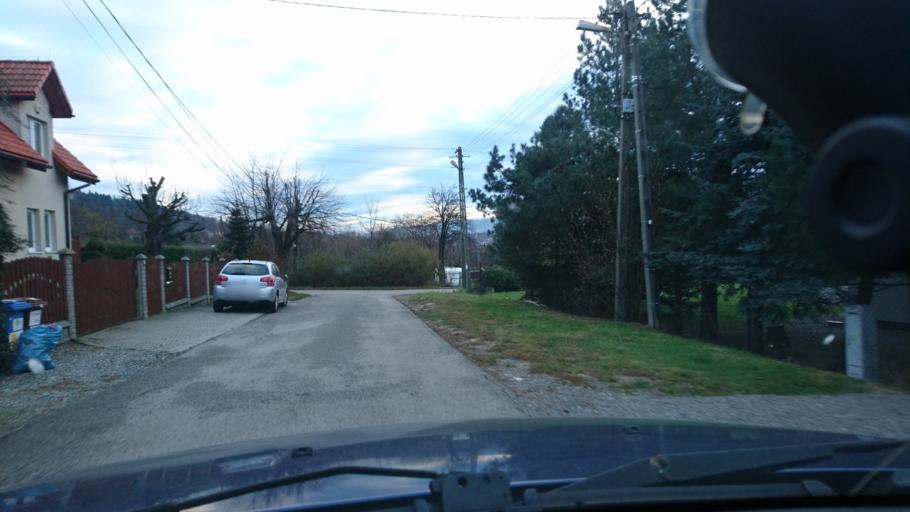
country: PL
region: Silesian Voivodeship
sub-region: Powiat bielski
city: Wilkowice
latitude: 49.7938
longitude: 19.0765
